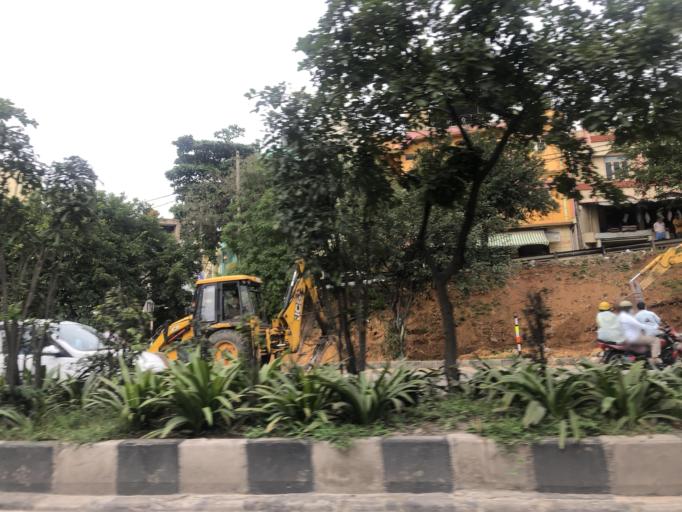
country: IN
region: Karnataka
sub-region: Bangalore Urban
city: Bangalore
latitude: 13.0070
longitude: 77.5267
